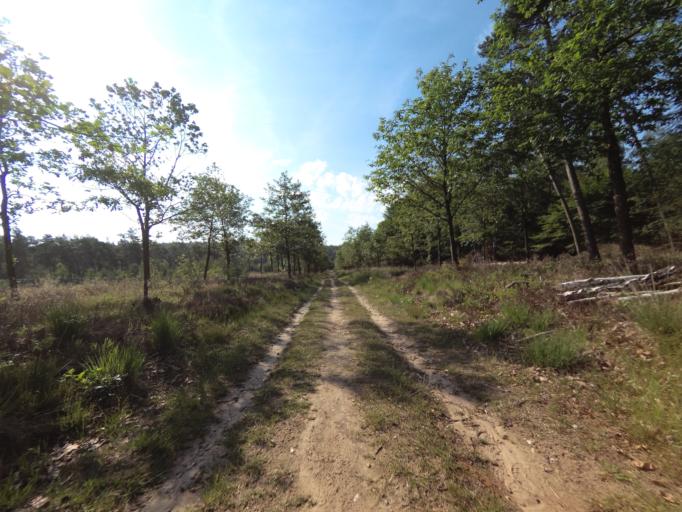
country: NL
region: Gelderland
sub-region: Gemeente Apeldoorn
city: Beekbergen
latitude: 52.1605
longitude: 5.8975
